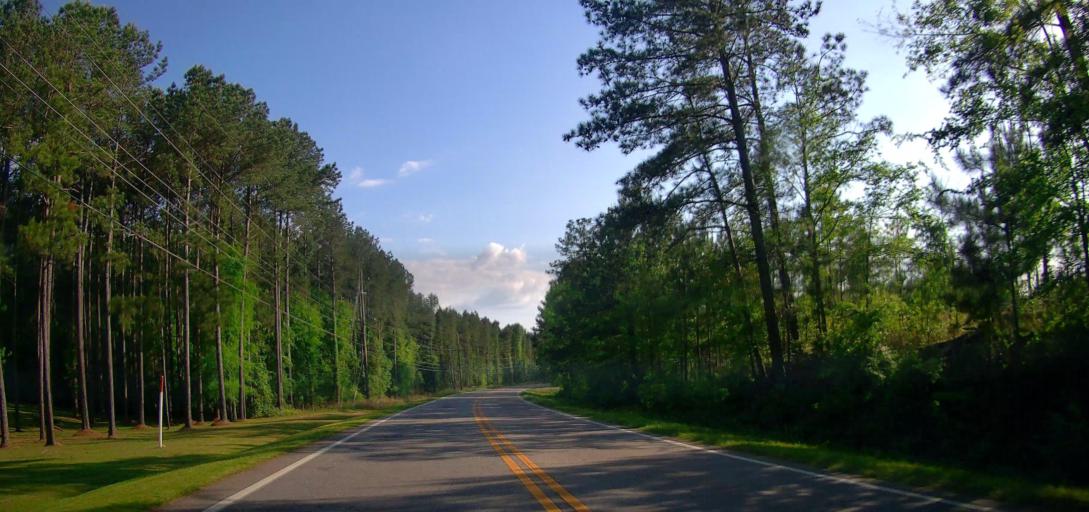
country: US
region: Georgia
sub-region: Putnam County
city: Eatonton
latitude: 33.2461
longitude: -83.3039
